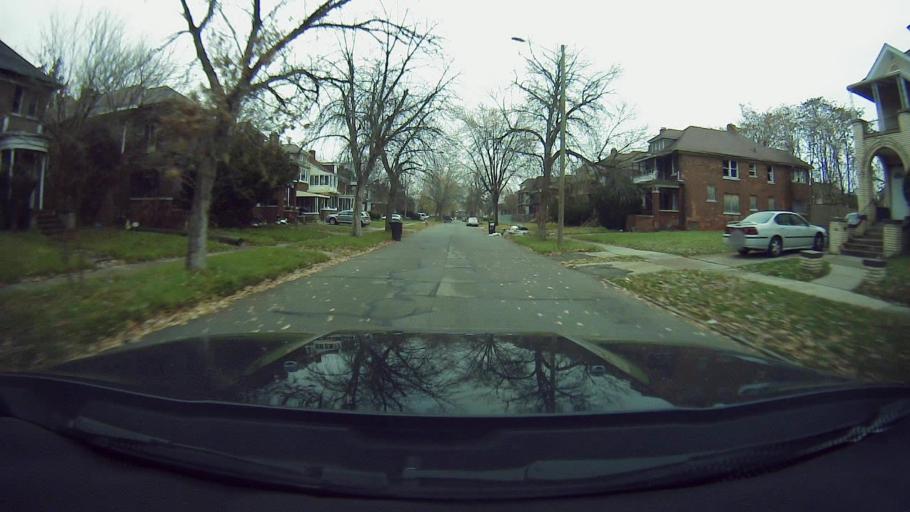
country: US
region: Michigan
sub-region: Wayne County
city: Highland Park
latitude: 42.4195
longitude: -83.1040
